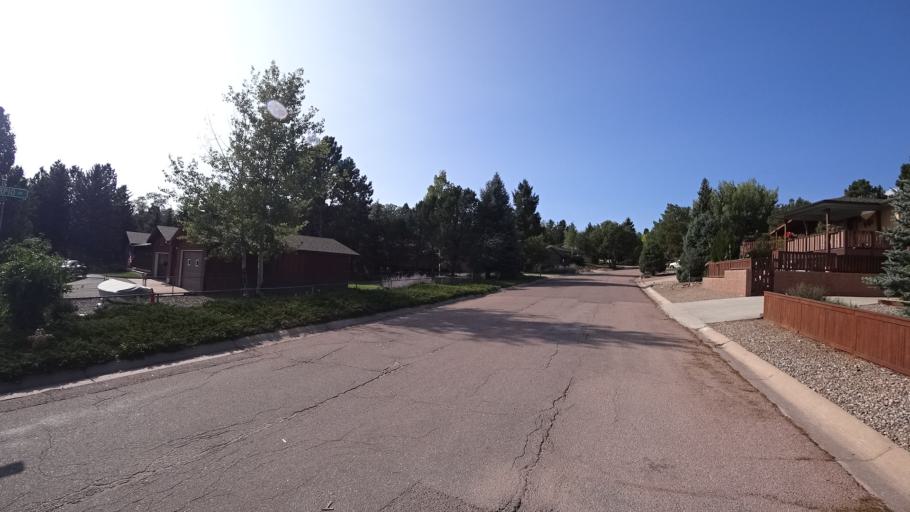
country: US
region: Colorado
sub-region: El Paso County
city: Colorado Springs
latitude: 38.8157
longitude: -104.8634
